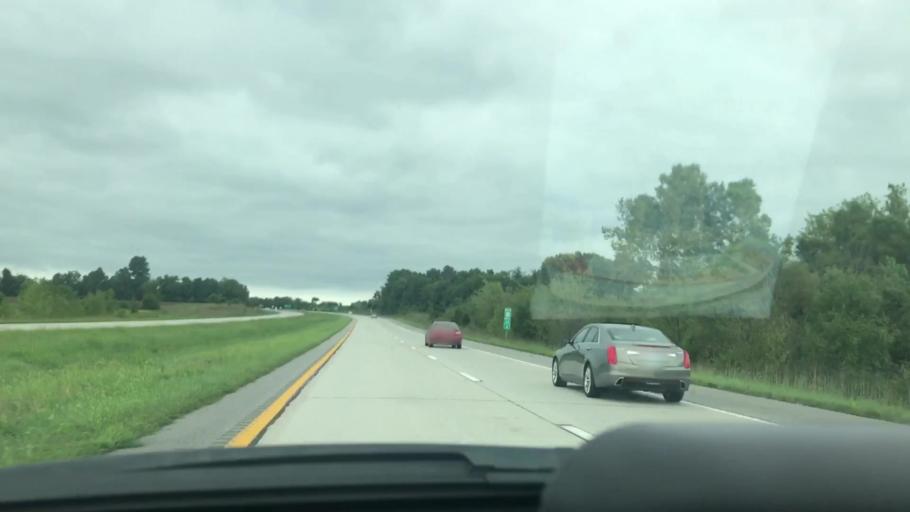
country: US
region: Missouri
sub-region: Greene County
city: Fair Grove
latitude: 37.4508
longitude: -93.1422
